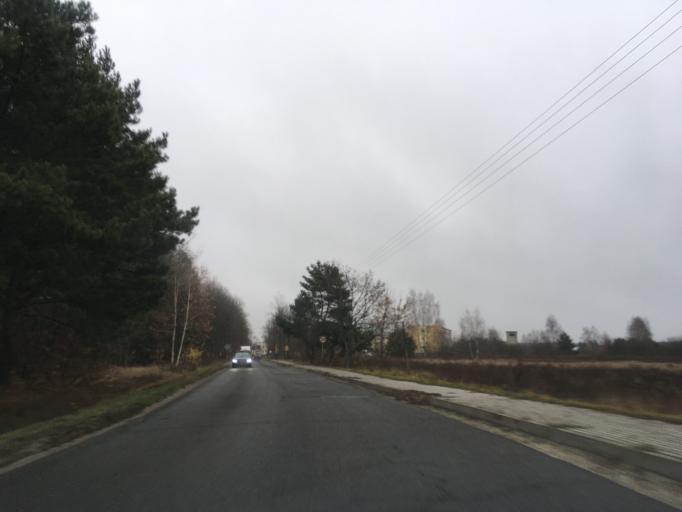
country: PL
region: Masovian Voivodeship
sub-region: Powiat piaseczynski
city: Lesznowola
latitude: 52.0697
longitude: 20.8839
